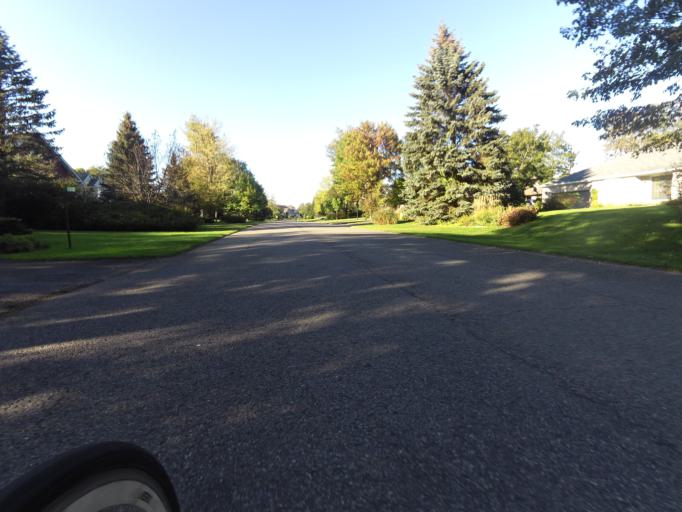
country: CA
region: Ontario
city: Bells Corners
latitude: 45.2208
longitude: -75.7007
